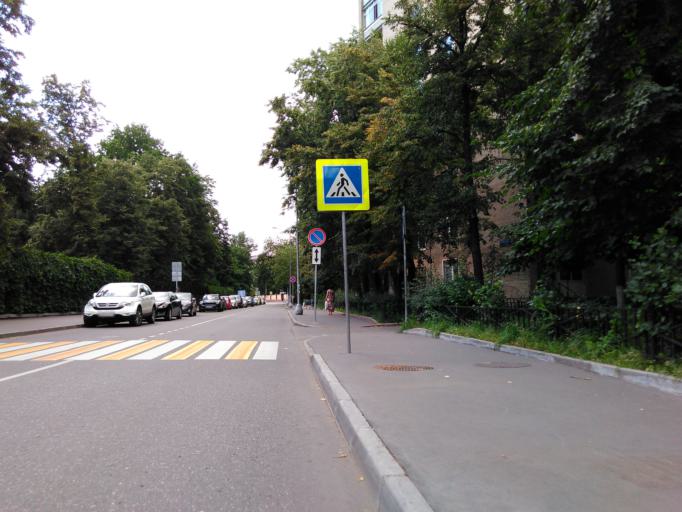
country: RU
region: Moskovskaya
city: Dorogomilovo
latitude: 55.7301
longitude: 37.5791
